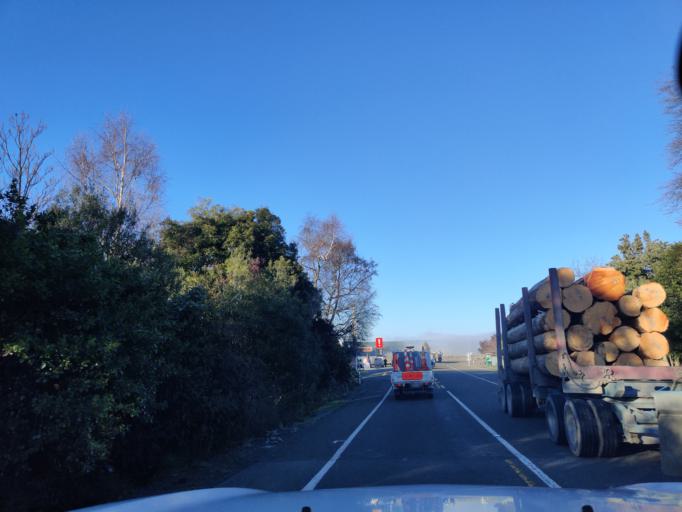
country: NZ
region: Waikato
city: Turangi
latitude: -38.9125
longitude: 175.8980
